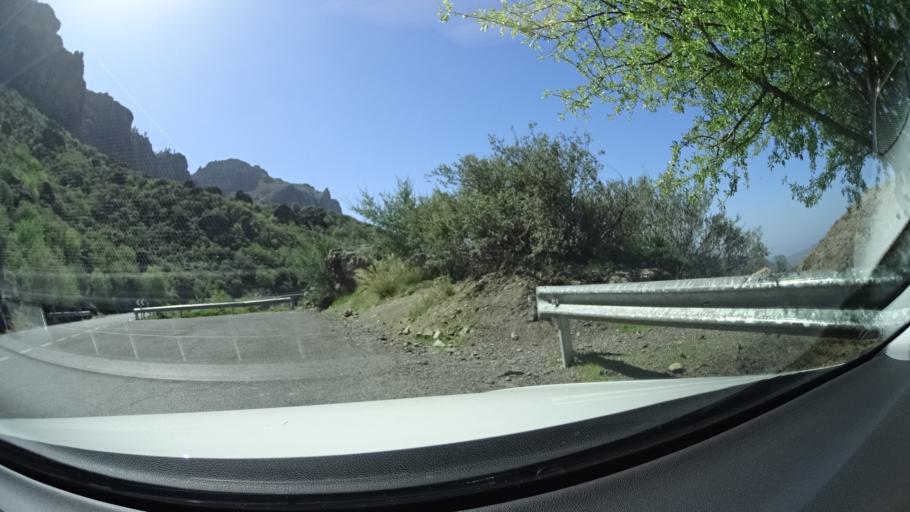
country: ES
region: Canary Islands
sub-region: Provincia de Las Palmas
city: Tejeda
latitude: 27.9764
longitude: -15.6170
